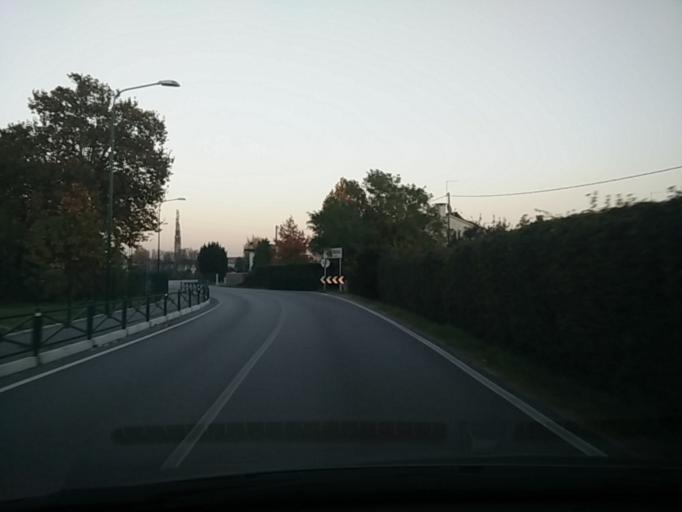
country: IT
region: Veneto
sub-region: Provincia di Treviso
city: Lancenigo-Villorba
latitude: 45.7100
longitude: 12.2670
